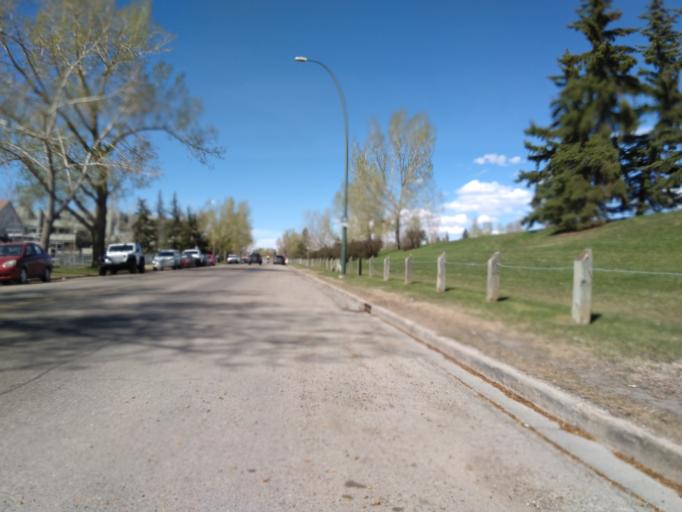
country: CA
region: Alberta
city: Calgary
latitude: 51.0142
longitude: -114.1597
